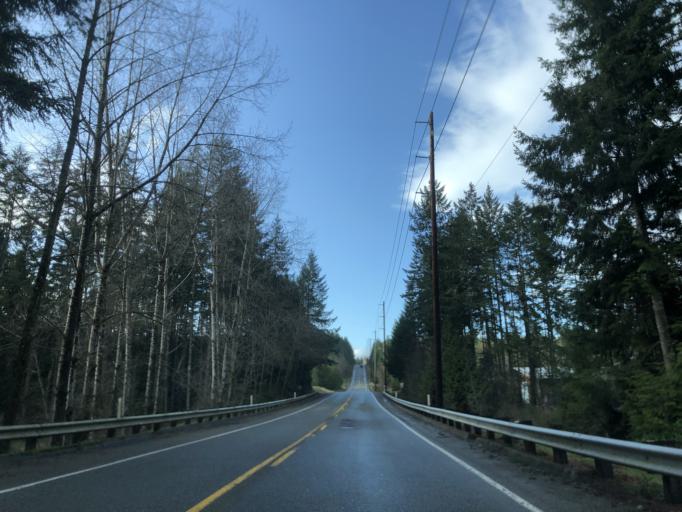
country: US
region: Washington
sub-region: Kitsap County
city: Poulsbo
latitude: 47.7696
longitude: -122.6528
